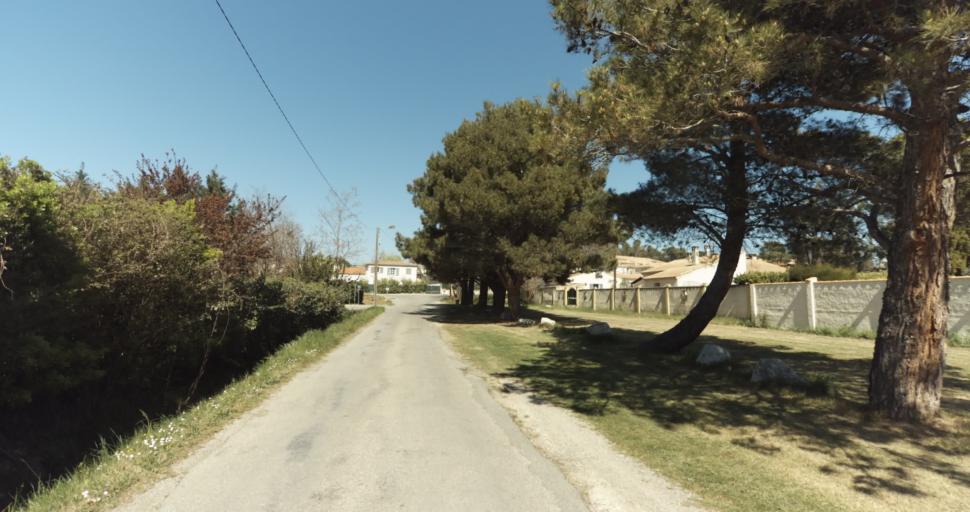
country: FR
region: Provence-Alpes-Cote d'Azur
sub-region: Departement des Bouches-du-Rhone
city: Pelissanne
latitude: 43.6335
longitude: 5.1610
